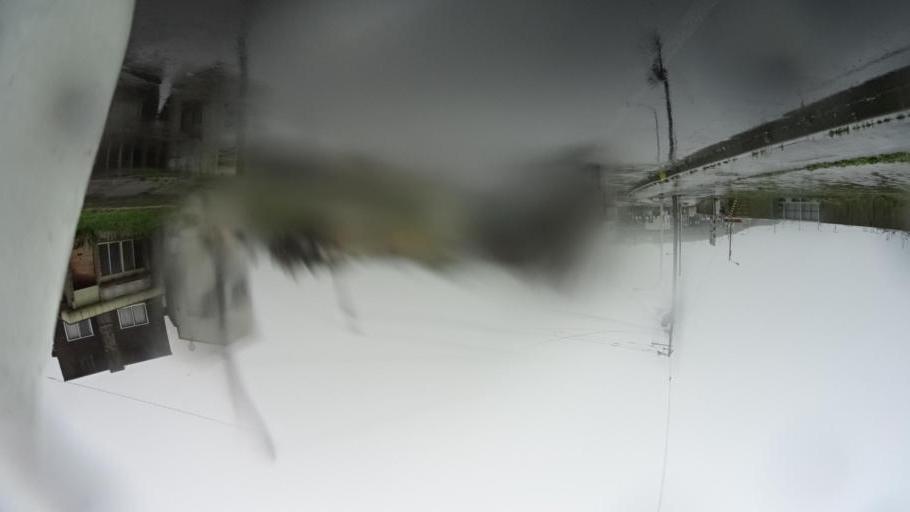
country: JP
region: Hokkaido
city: Nemuro
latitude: 43.2865
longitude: 145.5832
